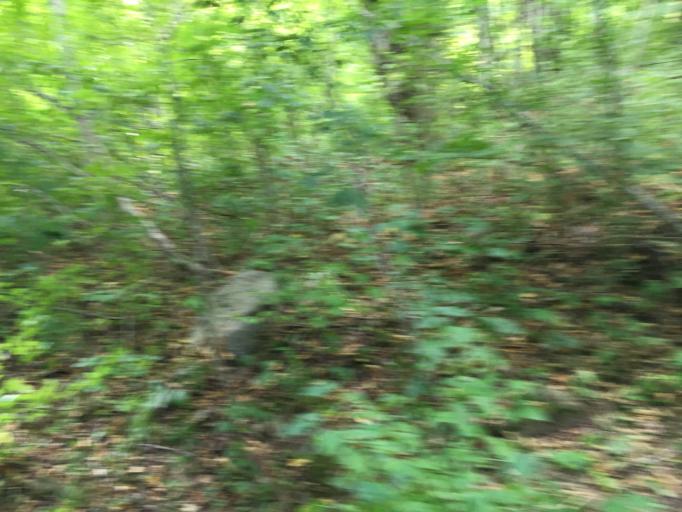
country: RU
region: Krasnodarskiy
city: Tuapse
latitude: 44.2584
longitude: 39.2178
